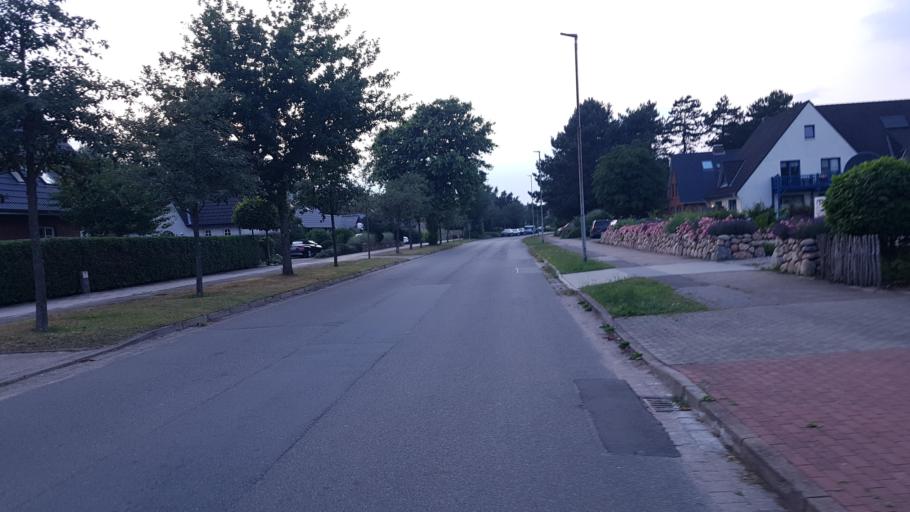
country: DE
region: Schleswig-Holstein
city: Sankt Peter-Ording
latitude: 54.2981
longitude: 8.6442
